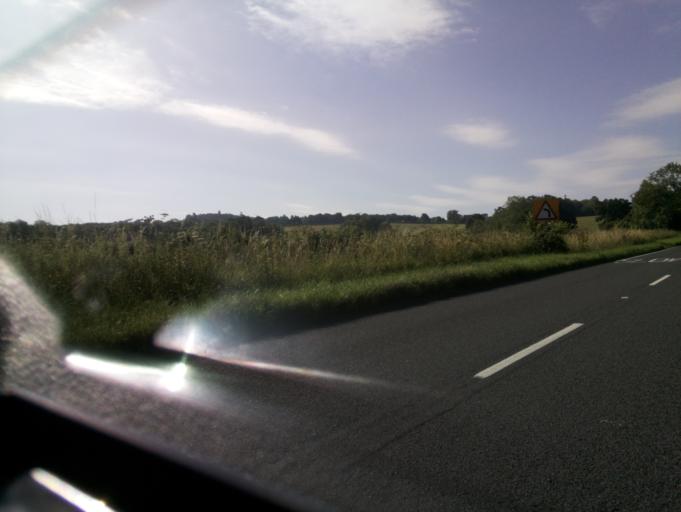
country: GB
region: England
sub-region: Oxfordshire
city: Faringdon
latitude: 51.6666
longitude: -1.5863
